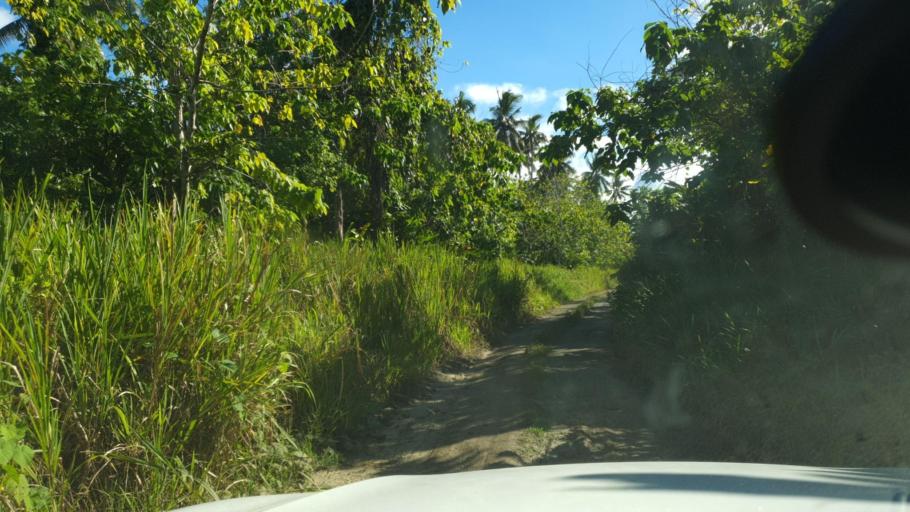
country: SB
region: Guadalcanal
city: Honiara
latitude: -9.4247
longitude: 160.1743
